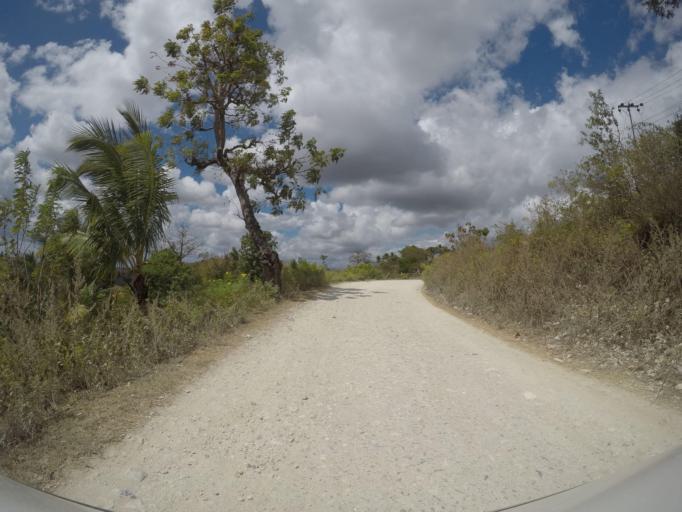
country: TL
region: Baucau
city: Baucau
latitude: -8.5276
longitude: 126.6973
